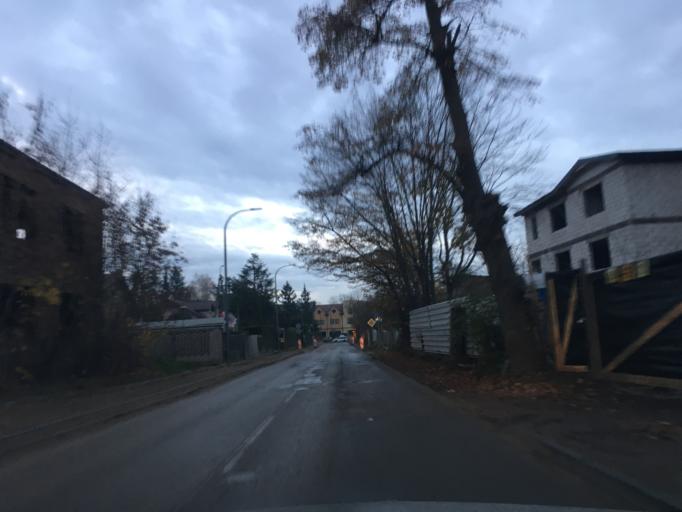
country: PL
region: Masovian Voivodeship
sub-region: Powiat piaseczynski
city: Piaseczno
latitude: 52.0506
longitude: 20.9881
